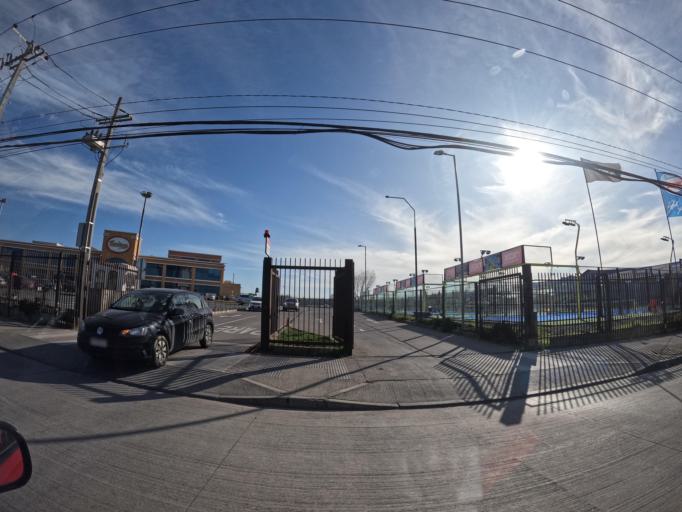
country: CL
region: Biobio
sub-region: Provincia de Concepcion
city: Concepcion
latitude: -36.7770
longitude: -73.0758
